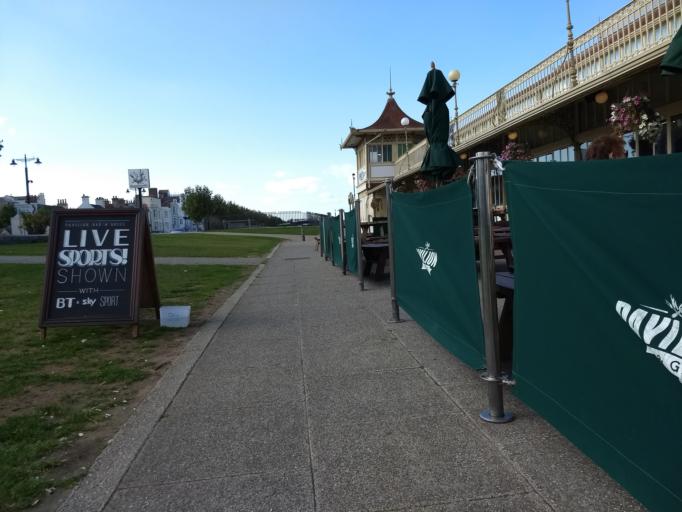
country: GB
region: England
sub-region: Isle of Wight
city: Ryde
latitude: 50.7318
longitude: -1.1563
